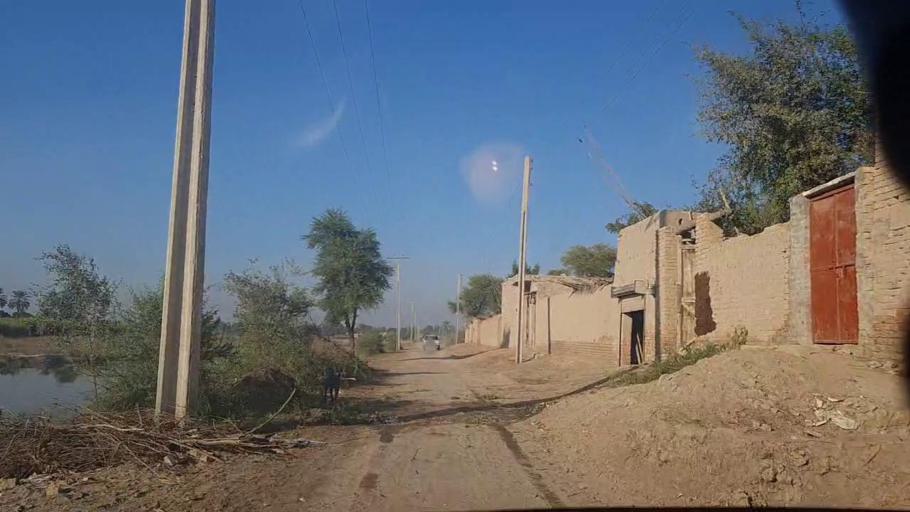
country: PK
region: Sindh
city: Sobhadero
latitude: 27.3824
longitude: 68.4168
